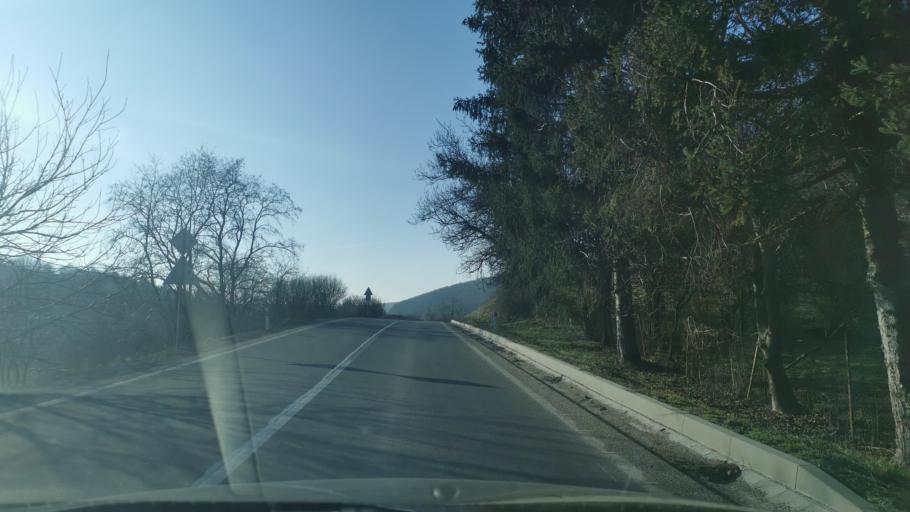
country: SK
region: Trenciansky
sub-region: Okres Myjava
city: Myjava
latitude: 48.7439
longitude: 17.4665
